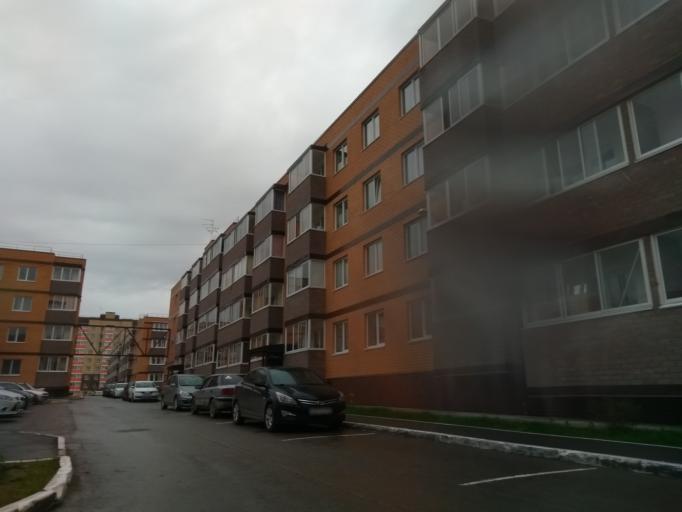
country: RU
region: Perm
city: Perm
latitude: 58.0005
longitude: 56.3390
